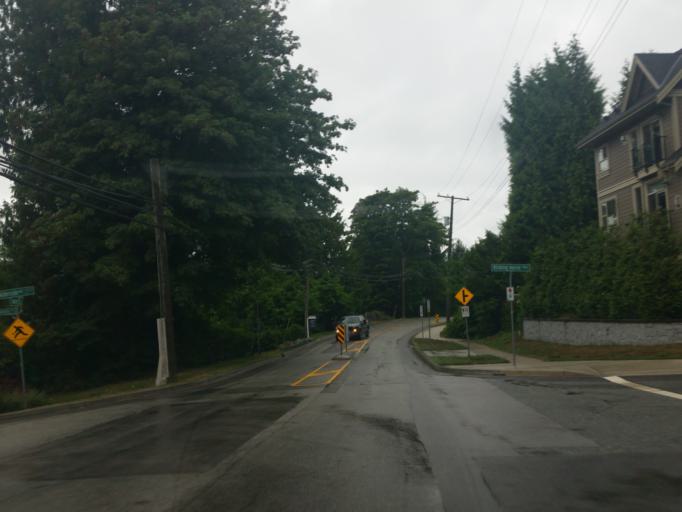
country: CA
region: British Columbia
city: Port Moody
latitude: 49.2911
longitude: -122.8456
